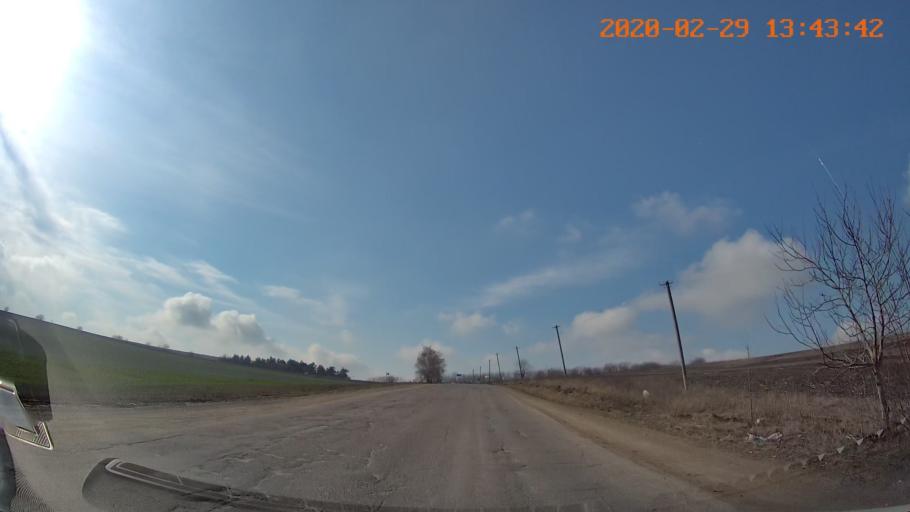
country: MD
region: Floresti
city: Leninskiy
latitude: 47.8392
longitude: 28.5286
